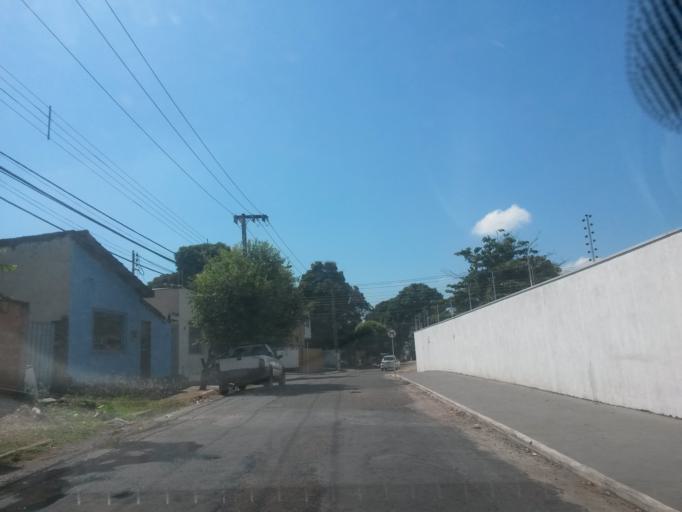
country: BR
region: Mato Grosso
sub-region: Cuiaba
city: Cuiaba
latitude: -15.5907
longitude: -56.0917
